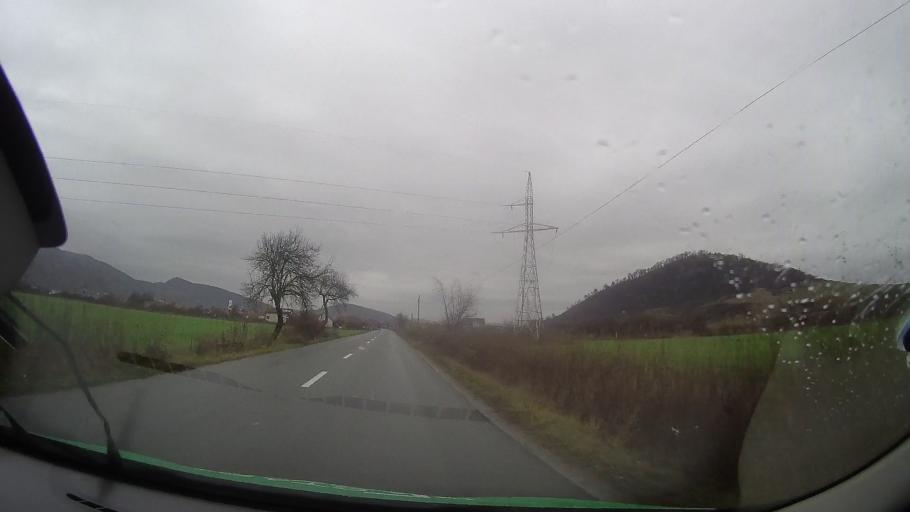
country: RO
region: Bistrita-Nasaud
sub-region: Municipiul Bistrita
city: Viisoara
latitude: 47.0647
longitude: 24.4370
